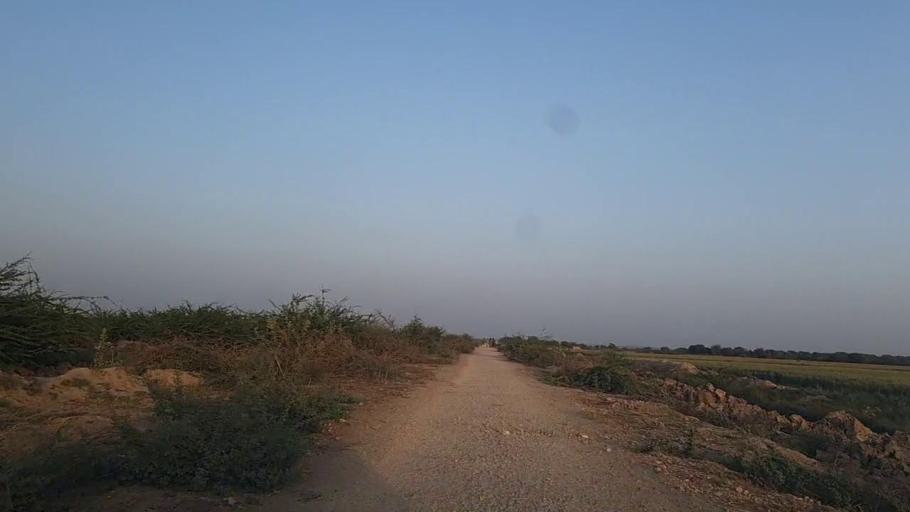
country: PK
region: Sindh
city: Naukot
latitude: 24.6966
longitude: 69.2677
